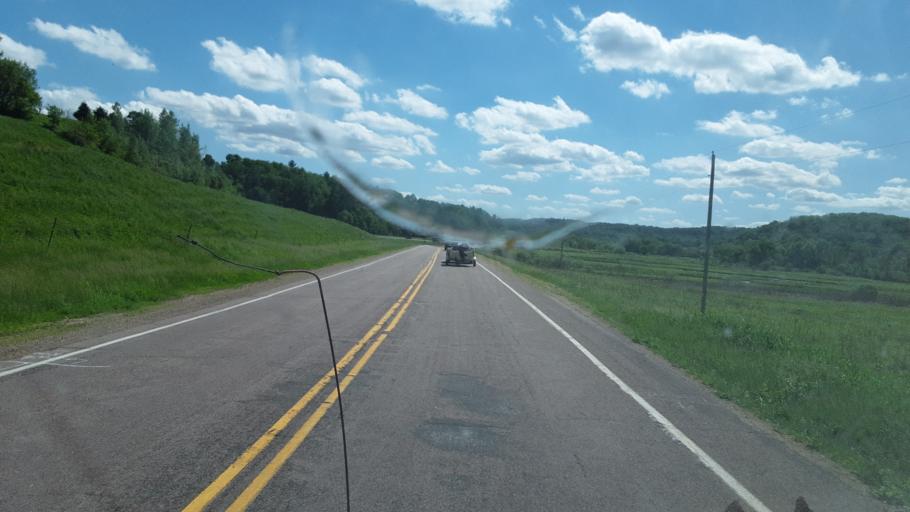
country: US
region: Wisconsin
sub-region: Richland County
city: Richland Center
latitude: 43.3861
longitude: -90.2487
